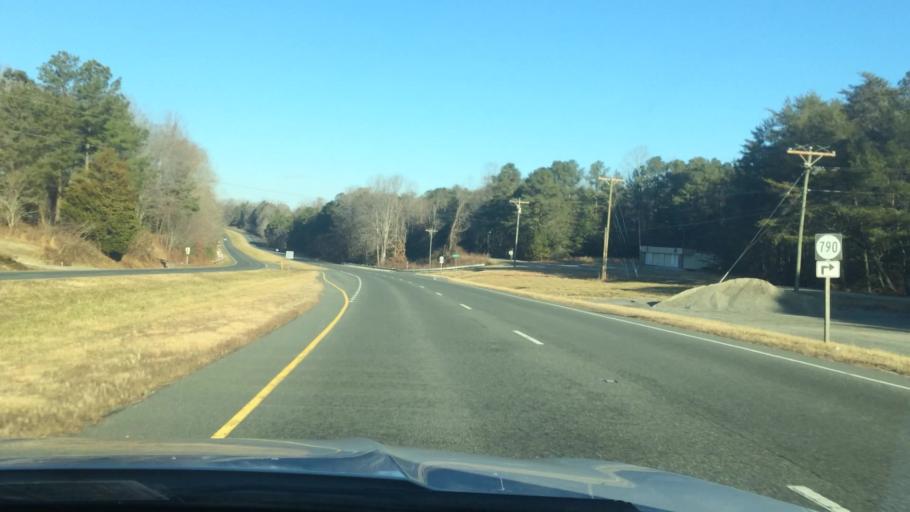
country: US
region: Virginia
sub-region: Lancaster County
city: Kilmarnock
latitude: 37.7388
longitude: -76.3942
